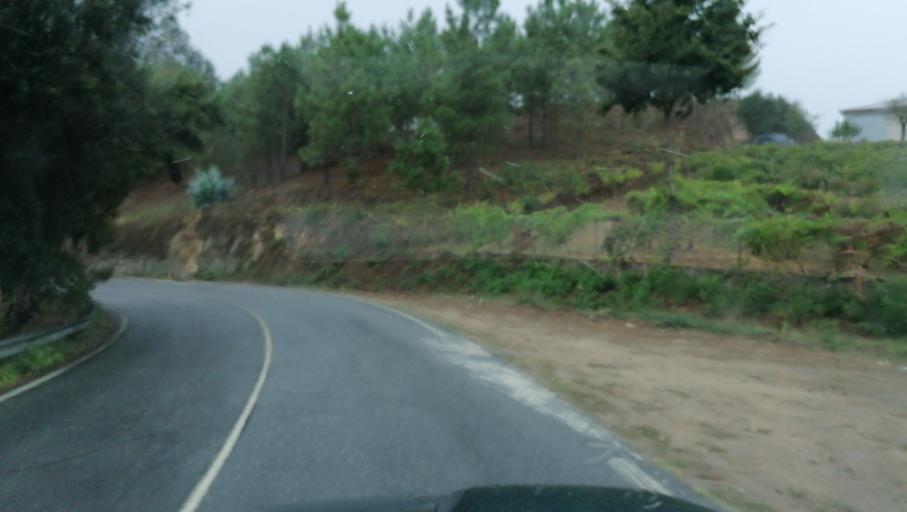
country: PT
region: Braga
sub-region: Cabeceiras de Basto
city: Cabeceiras de Basto
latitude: 41.4914
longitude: -7.9484
